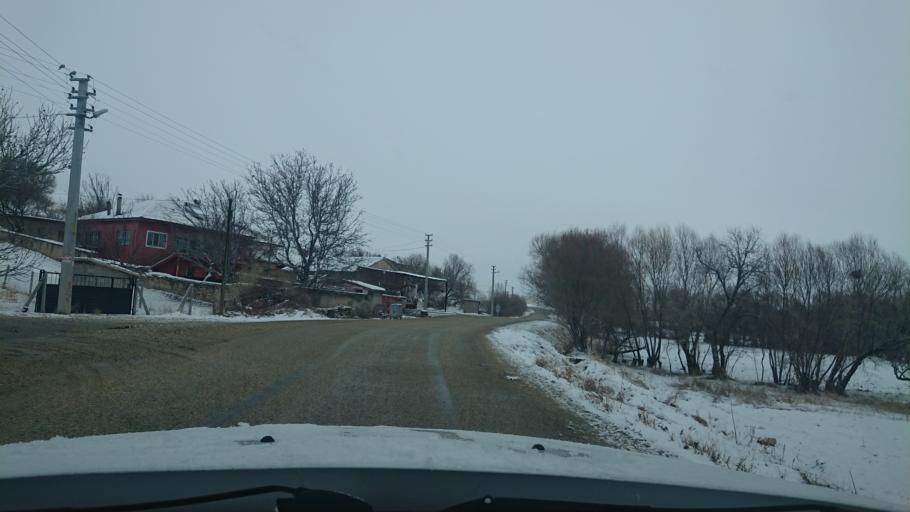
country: TR
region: Aksaray
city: Agacoren
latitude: 38.7593
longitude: 33.8685
